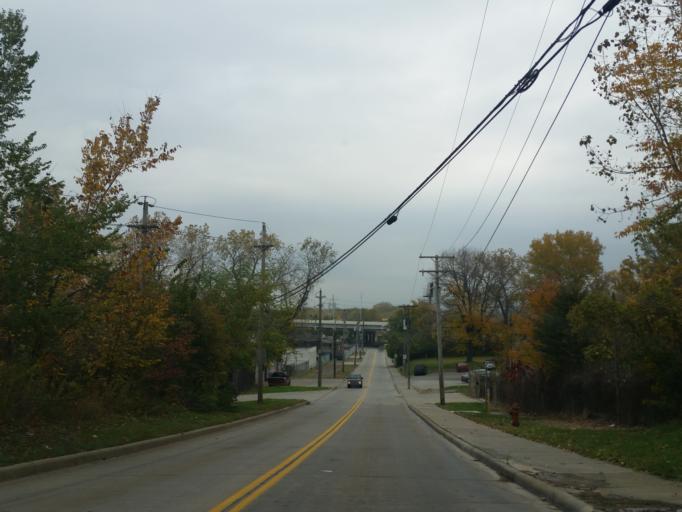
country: US
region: Ohio
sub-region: Cuyahoga County
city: Brooklyn Heights
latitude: 41.4458
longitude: -81.6929
